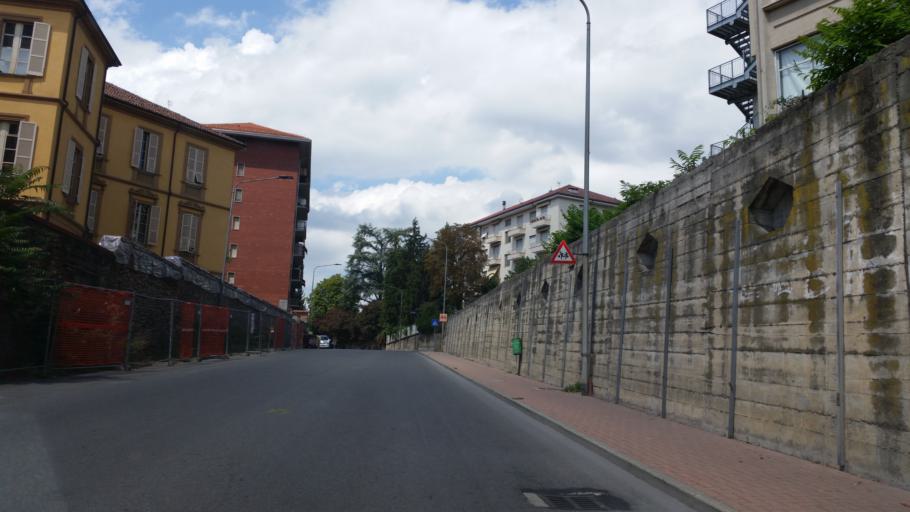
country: IT
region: Piedmont
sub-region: Provincia di Alessandria
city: Acqui Terme
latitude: 44.6742
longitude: 8.4752
